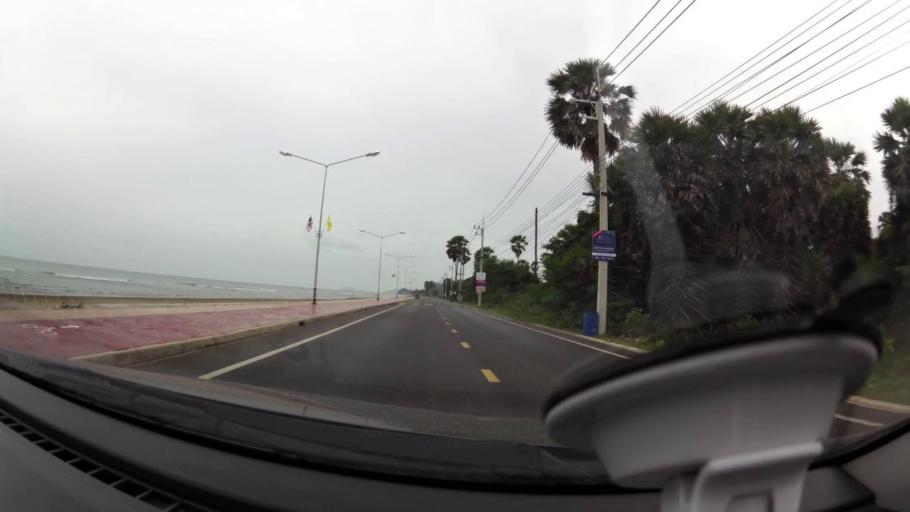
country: TH
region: Prachuap Khiri Khan
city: Pran Buri
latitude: 12.3759
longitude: 100.0002
